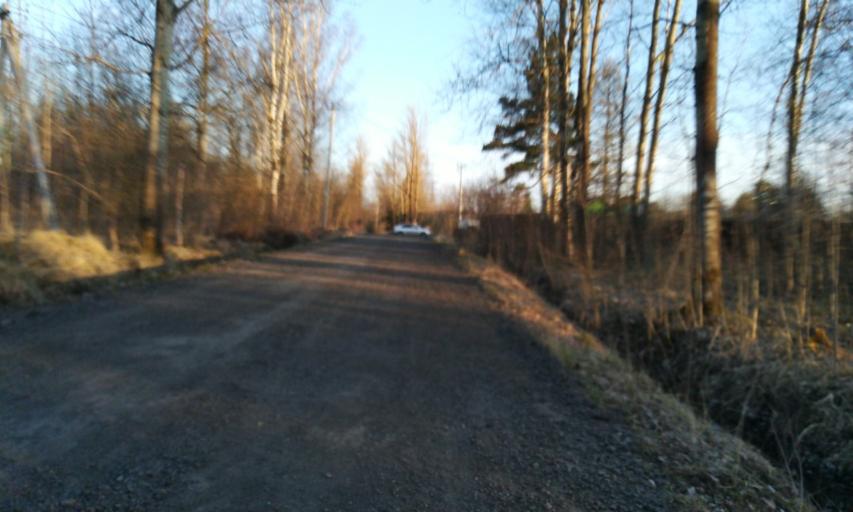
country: RU
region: Leningrad
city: Novoye Devyatkino
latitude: 60.0863
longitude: 30.4581
